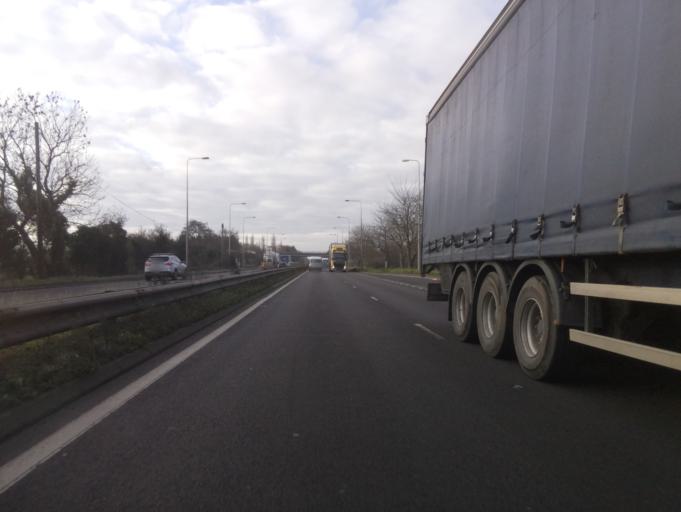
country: GB
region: England
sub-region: Staffordshire
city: Alrewas
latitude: 52.7184
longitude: -1.7571
